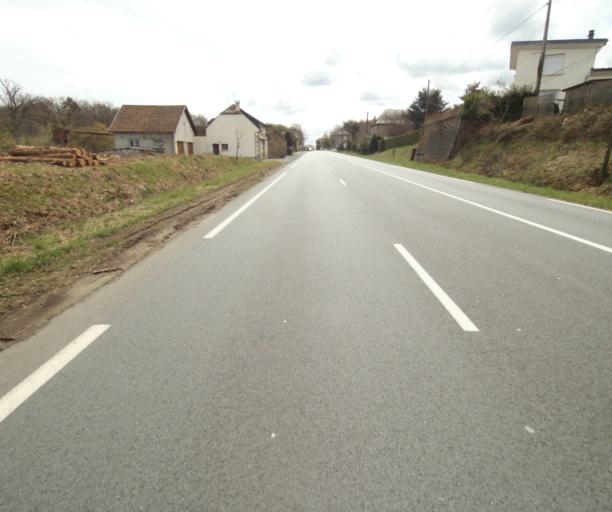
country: FR
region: Limousin
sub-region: Departement de la Correze
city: Sainte-Fortunade
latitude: 45.2028
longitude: 1.8296
